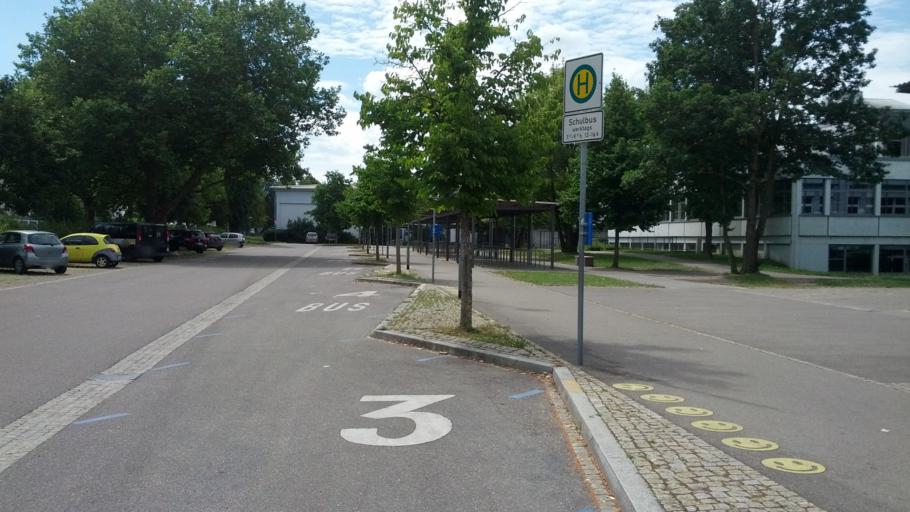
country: DE
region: Baden-Wuerttemberg
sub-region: Freiburg Region
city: Bad Krozingen
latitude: 47.9114
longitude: 7.6974
